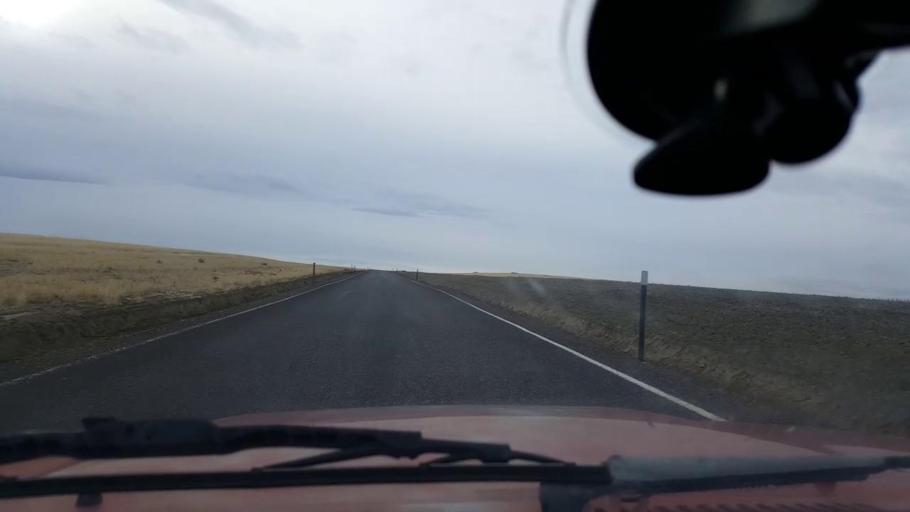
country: US
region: Washington
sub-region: Asotin County
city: Clarkston Heights-Vineland
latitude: 46.3553
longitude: -117.2240
